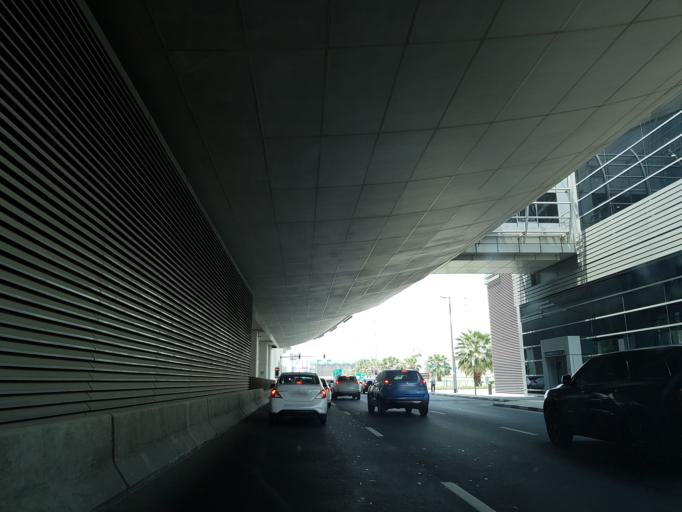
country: AE
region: Ash Shariqah
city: Sharjah
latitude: 25.2436
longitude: 55.3161
